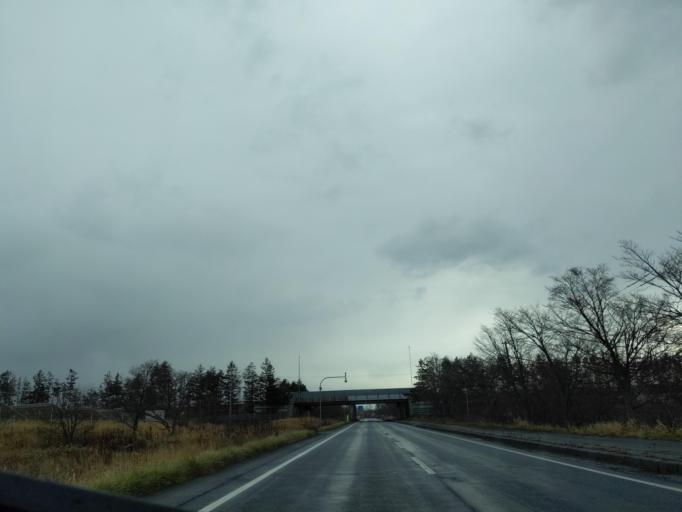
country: JP
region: Hokkaido
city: Ebetsu
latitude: 43.1050
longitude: 141.5965
